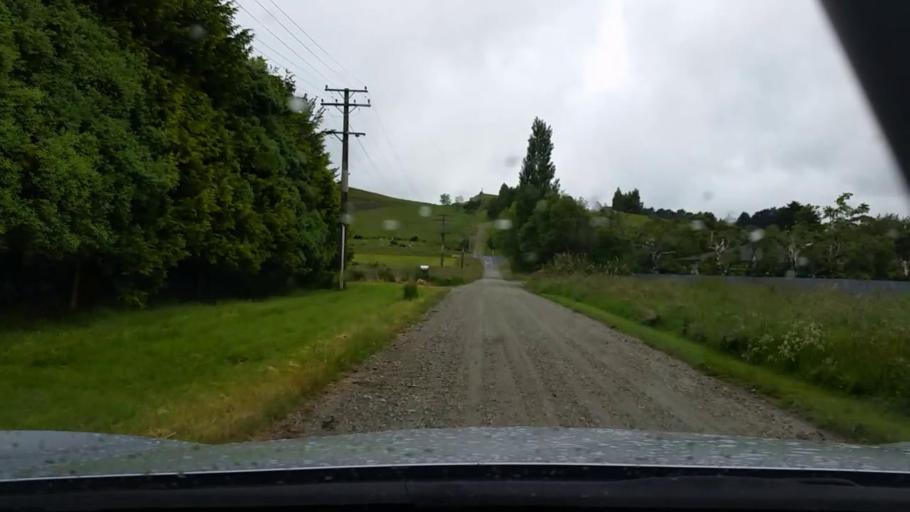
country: NZ
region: Southland
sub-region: Gore District
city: Gore
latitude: -46.0808
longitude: 168.9535
